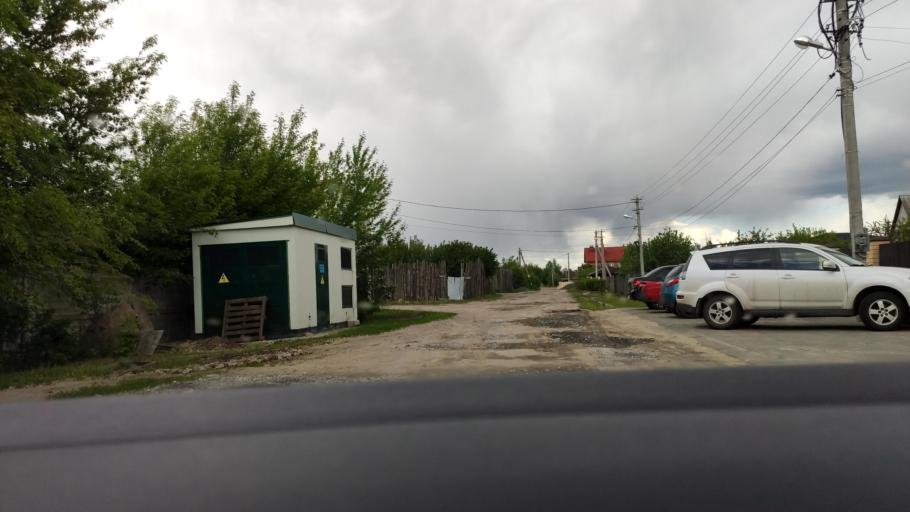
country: RU
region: Voronezj
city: Somovo
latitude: 51.6827
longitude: 39.3100
